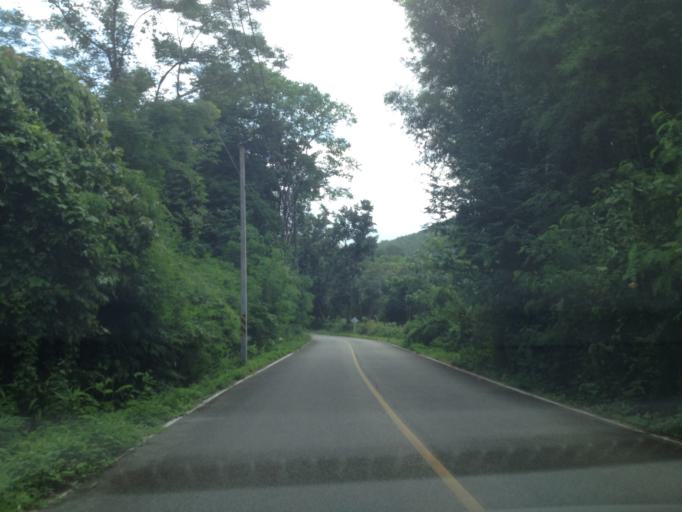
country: TH
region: Chiang Mai
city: Hang Dong
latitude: 18.7558
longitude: 98.9052
